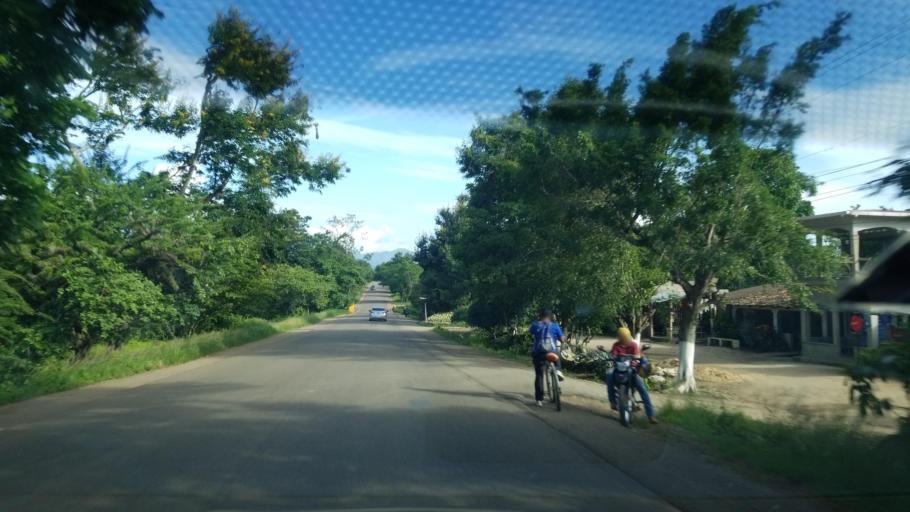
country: HN
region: El Paraiso
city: Arauli
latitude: 13.9462
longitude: -86.5597
